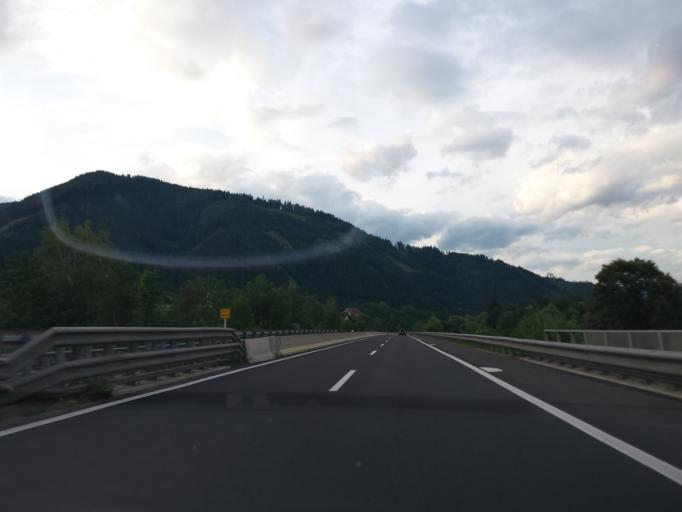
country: AT
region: Styria
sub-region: Politischer Bezirk Leoben
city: Kraubath an der Mur
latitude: 47.3099
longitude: 14.9504
